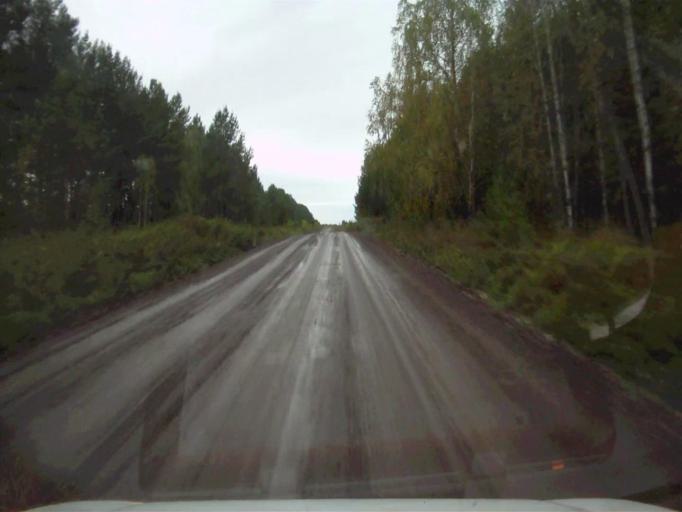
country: RU
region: Chelyabinsk
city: Nyazepetrovsk
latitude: 56.1429
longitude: 59.2884
